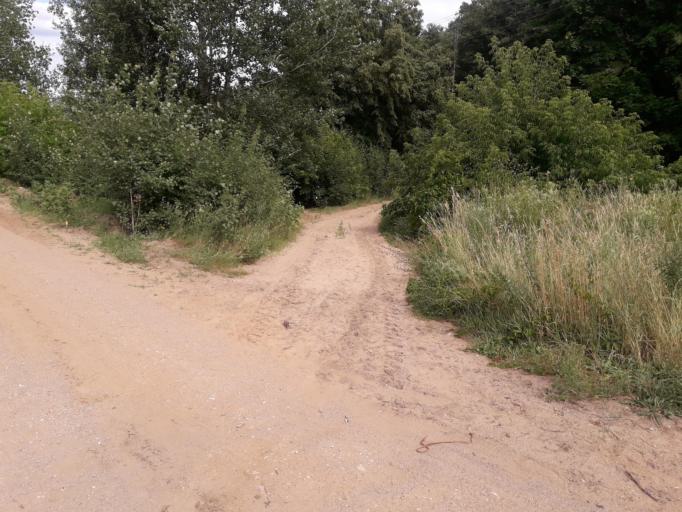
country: LT
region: Alytaus apskritis
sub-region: Alytaus rajonas
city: Daugai
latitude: 54.1644
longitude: 24.1969
